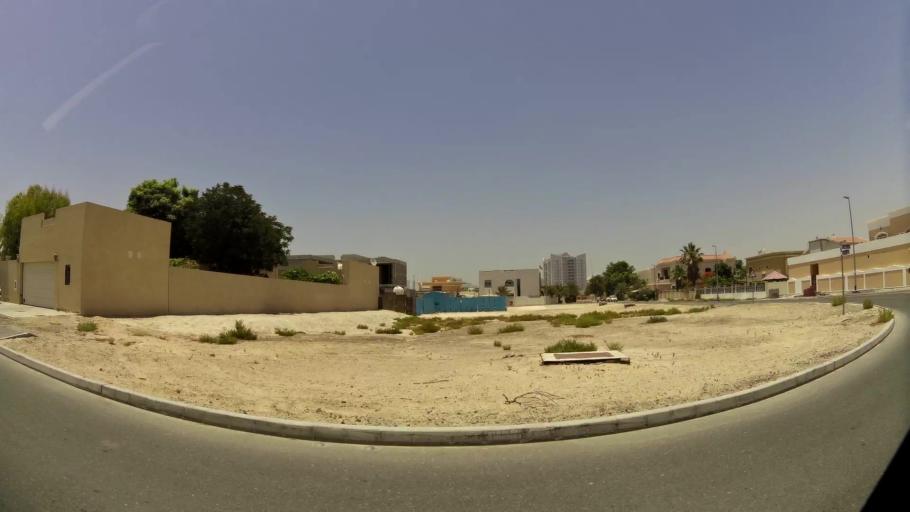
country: AE
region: Dubai
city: Dubai
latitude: 25.1009
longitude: 55.1987
